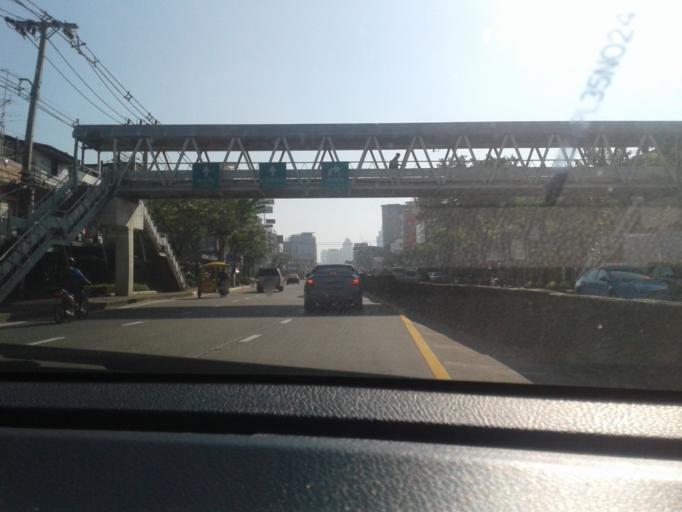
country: TH
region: Bangkok
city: Thon Buri
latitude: 13.7281
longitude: 100.4825
